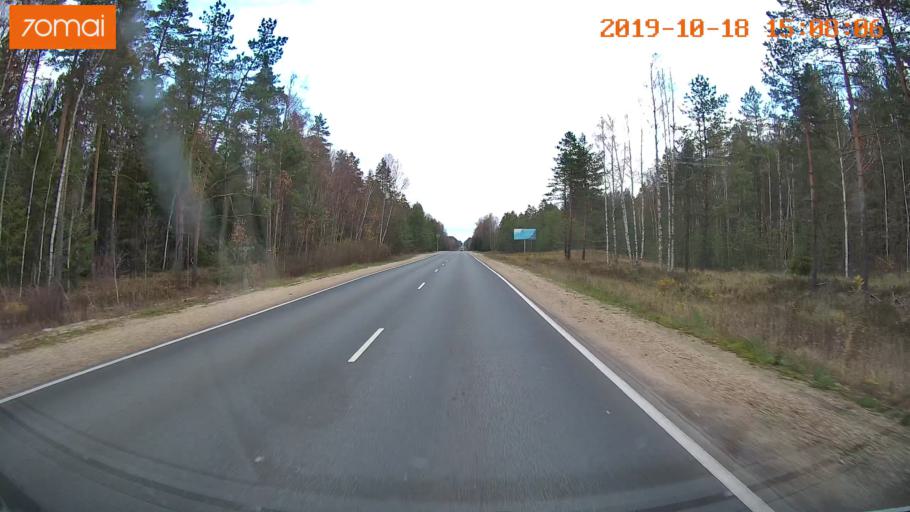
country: RU
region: Vladimir
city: Gus'-Khrustal'nyy
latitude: 55.5477
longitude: 40.6070
